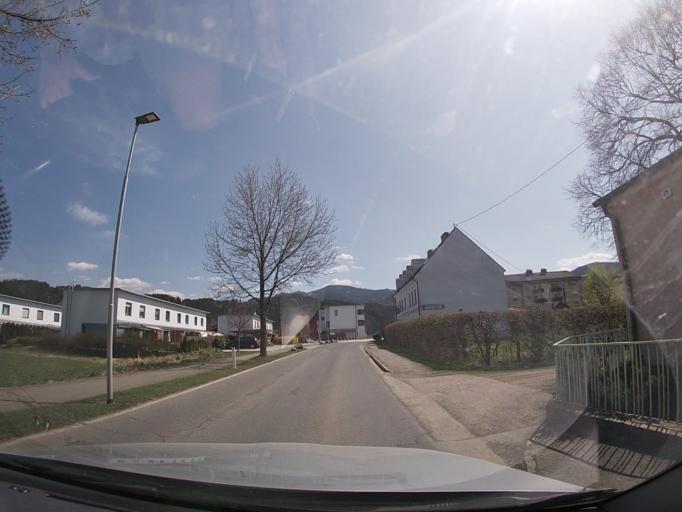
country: AT
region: Styria
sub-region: Politischer Bezirk Murtal
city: Apfelberg
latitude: 47.2064
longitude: 14.8335
